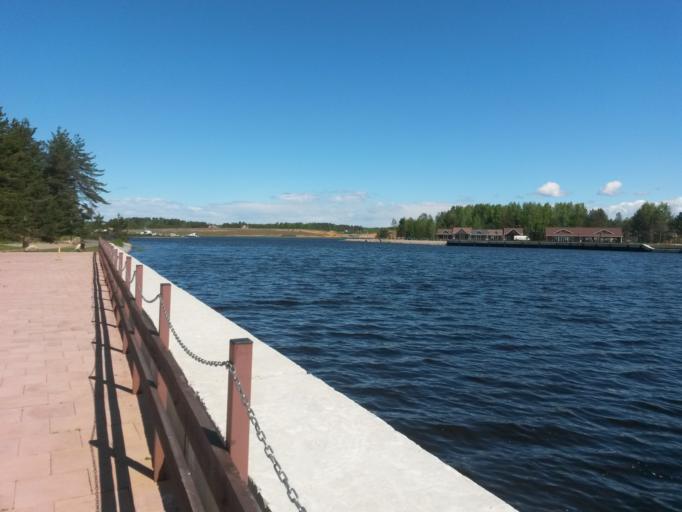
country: RU
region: Jaroslavl
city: Borok
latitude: 58.0607
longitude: 38.3510
